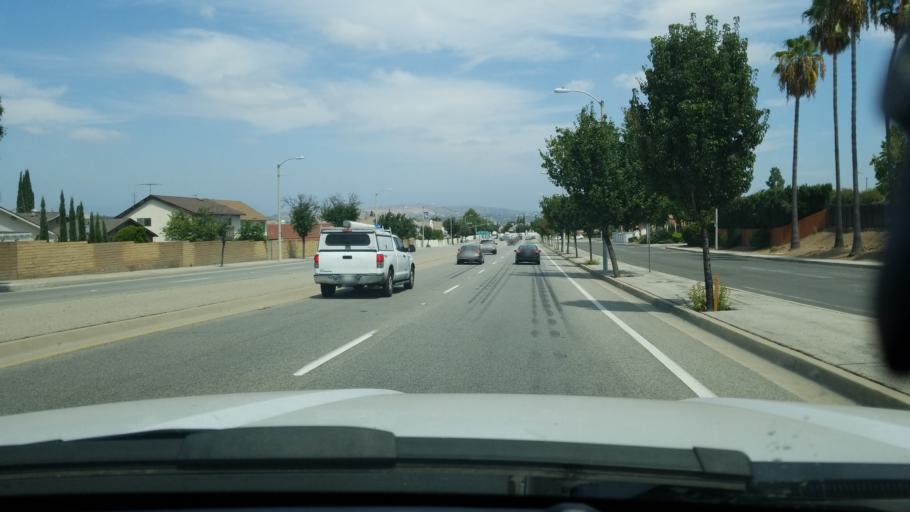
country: US
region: California
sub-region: Los Angeles County
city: Hacienda Heights
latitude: 33.9885
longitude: -117.9478
